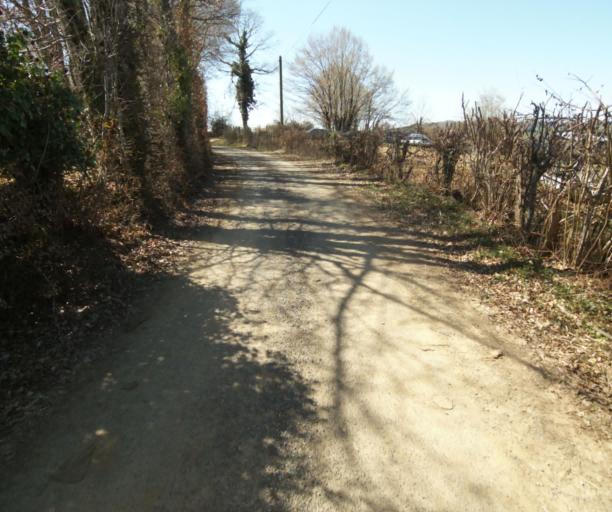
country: FR
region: Limousin
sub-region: Departement de la Correze
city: Chamboulive
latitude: 45.4638
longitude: 1.6682
